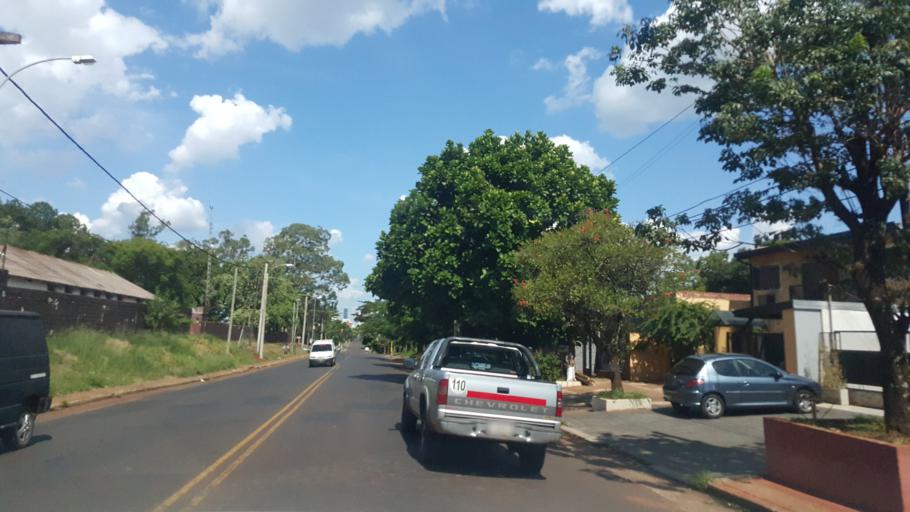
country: AR
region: Misiones
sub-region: Departamento de Capital
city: Posadas
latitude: -27.3654
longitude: -55.9180
